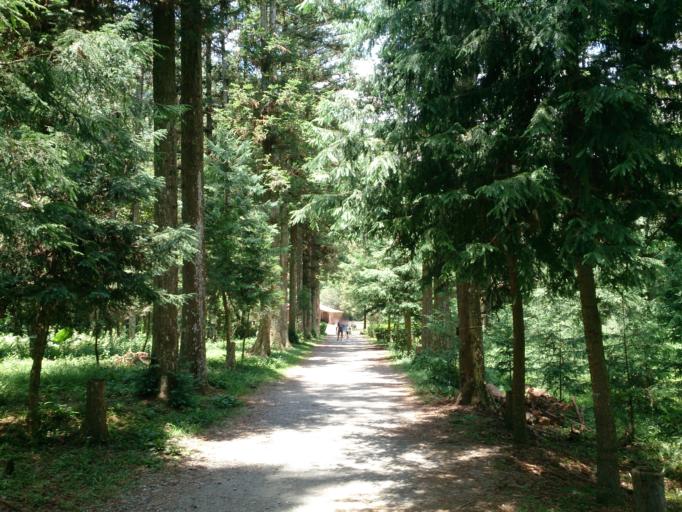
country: TW
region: Taiwan
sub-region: Nantou
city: Puli
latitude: 24.0899
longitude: 121.0315
